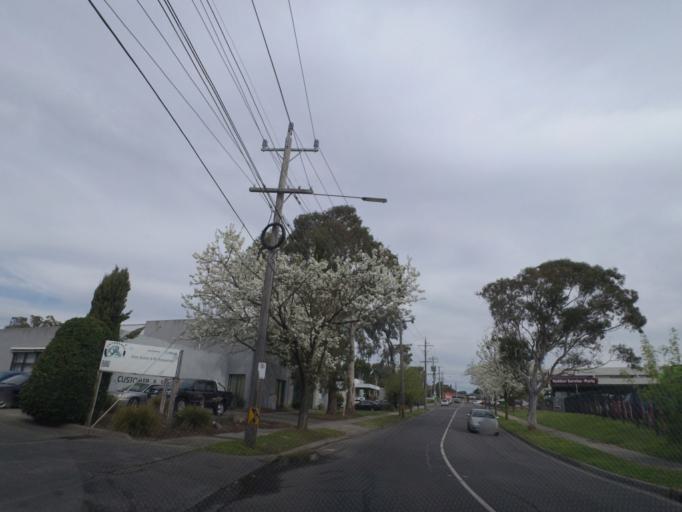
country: AU
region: Victoria
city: Forest Hill
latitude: -37.8350
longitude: 145.1883
